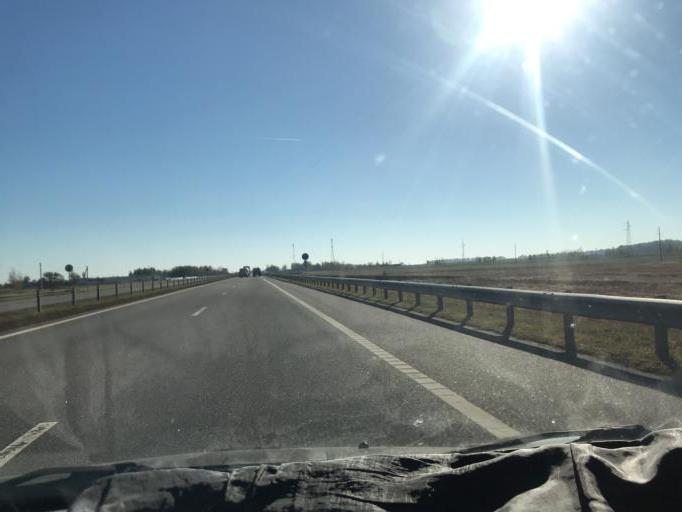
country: BY
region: Mogilev
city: Yalizava
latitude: 53.2539
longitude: 28.9152
